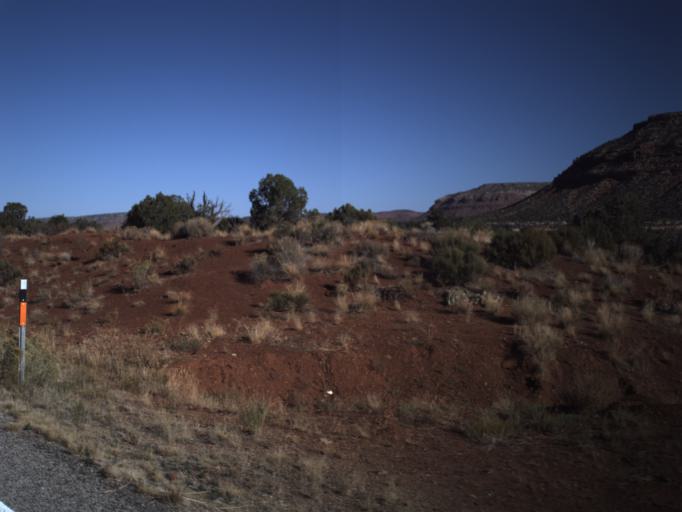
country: US
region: Utah
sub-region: San Juan County
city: Blanding
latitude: 37.6021
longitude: -110.0597
